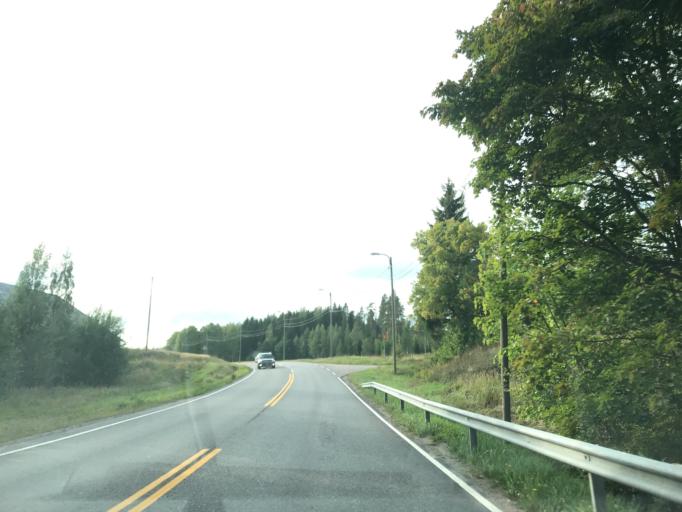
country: FI
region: Uusimaa
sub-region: Helsinki
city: Kirkkonummi
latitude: 60.2046
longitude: 24.5008
